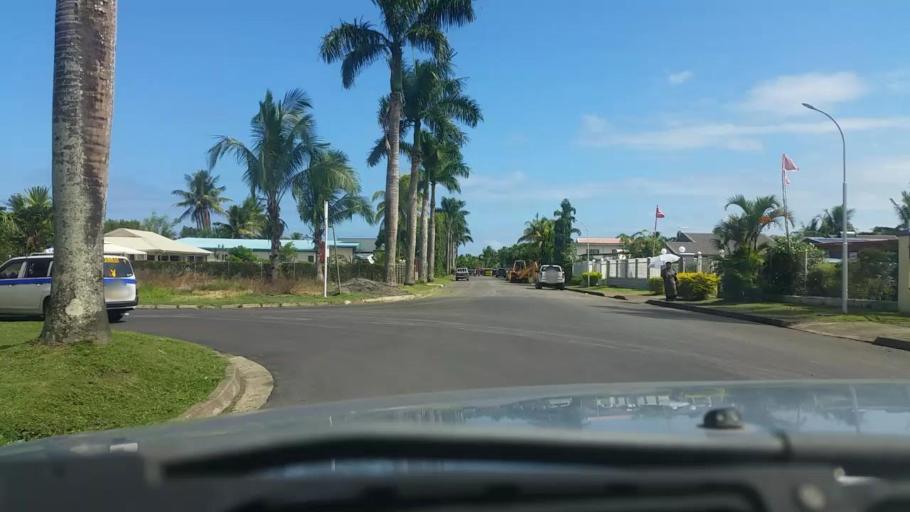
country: FJ
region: Central
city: Suva
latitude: -18.1299
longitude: 178.4647
